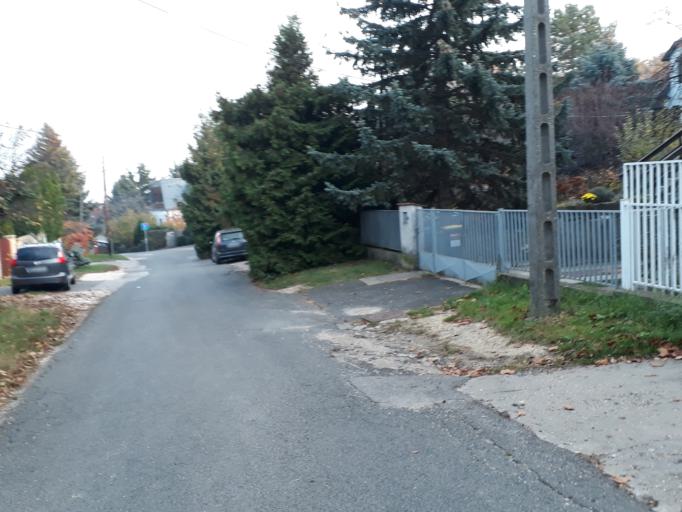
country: HU
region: Pest
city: Budaors
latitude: 47.4758
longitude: 18.9782
